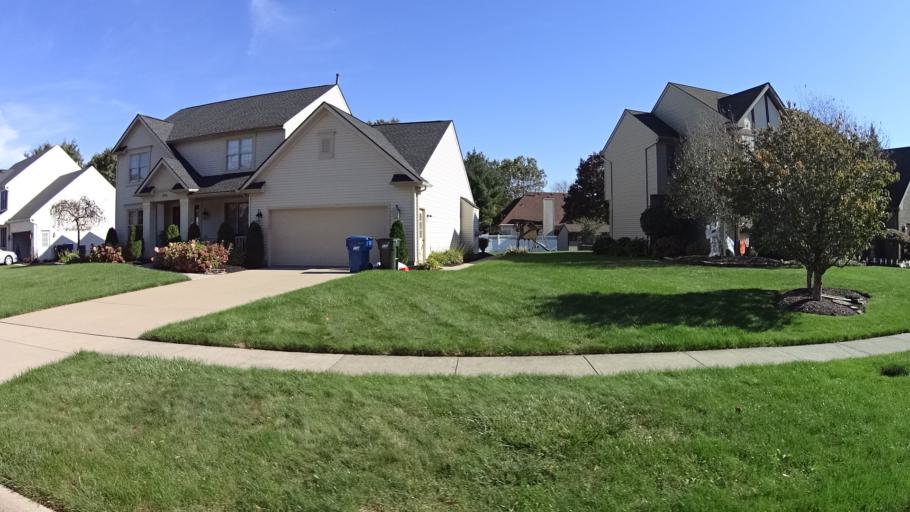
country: US
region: Ohio
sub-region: Lorain County
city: Amherst
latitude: 41.3944
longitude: -82.2440
